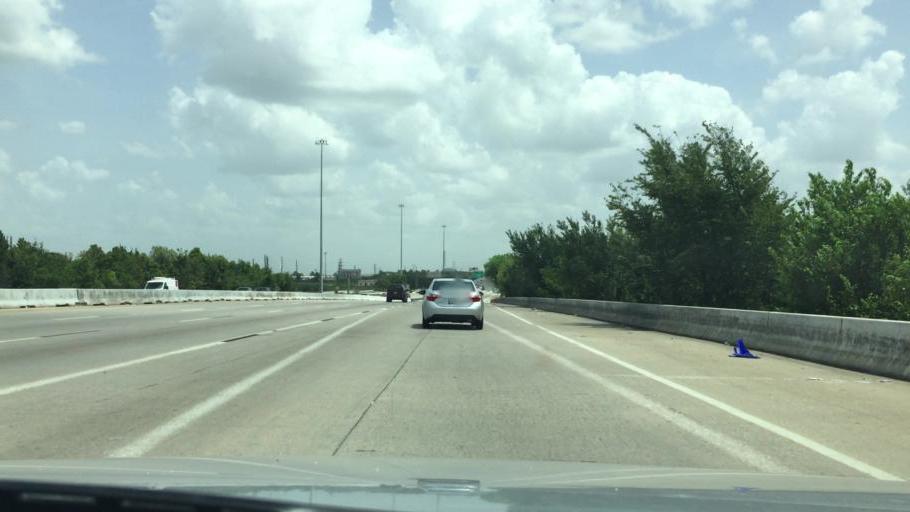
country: US
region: Texas
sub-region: Harris County
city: Hudson
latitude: 29.9527
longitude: -95.5373
